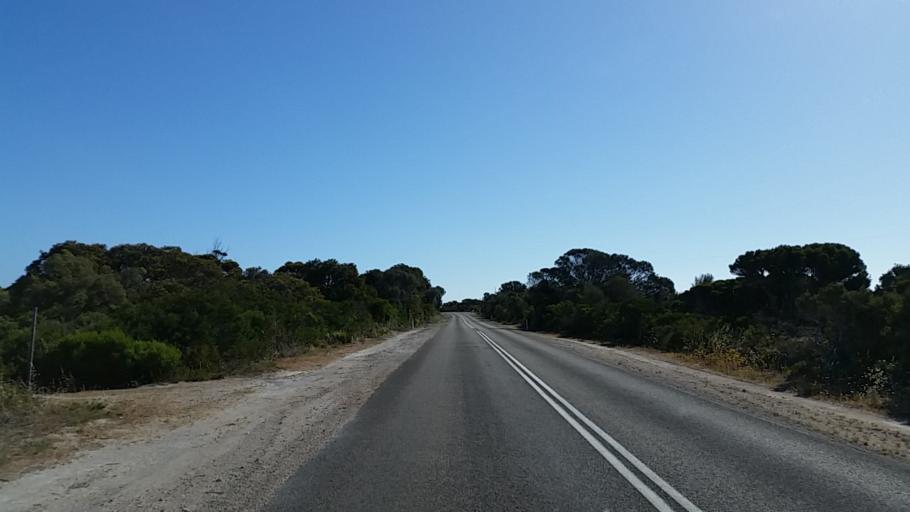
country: AU
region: South Australia
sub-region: Yorke Peninsula
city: Honiton
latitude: -35.2463
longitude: 136.9717
